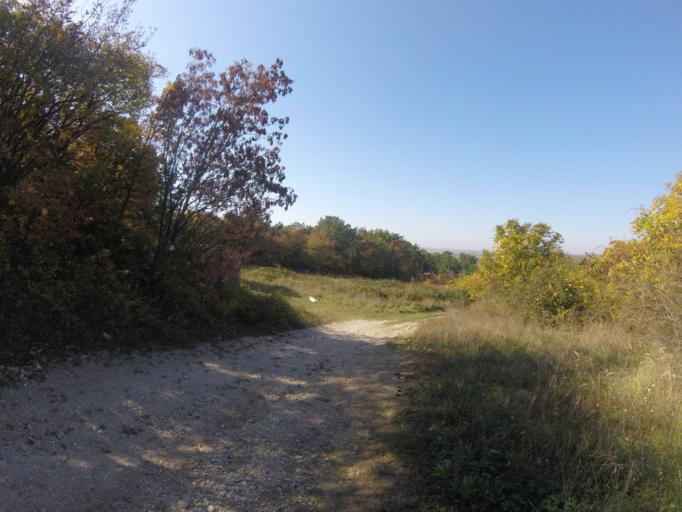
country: HU
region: Zala
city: Gyenesdias
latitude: 46.7808
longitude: 17.2898
